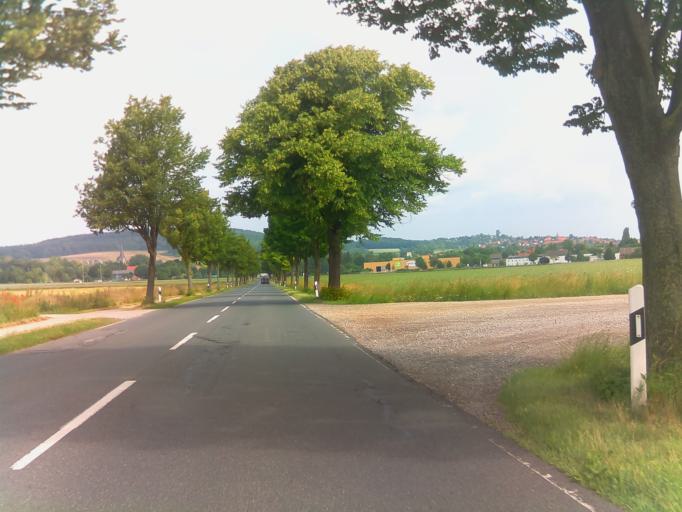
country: DE
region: Lower Saxony
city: Pattensen
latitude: 52.2259
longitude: 9.6820
